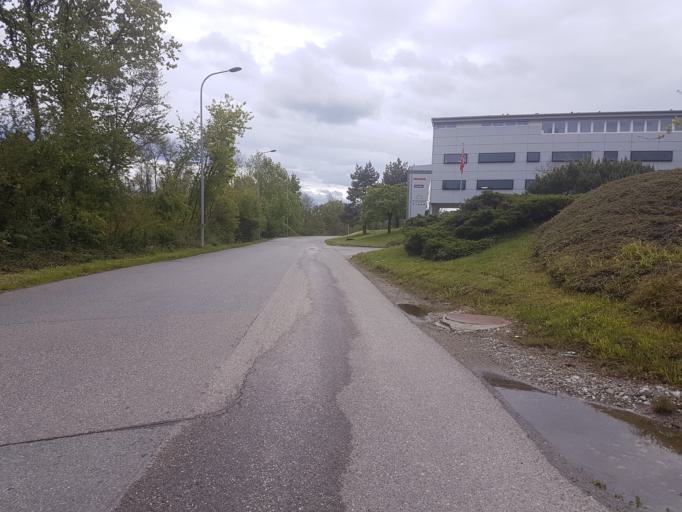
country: CH
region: Vaud
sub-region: Morges District
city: Preverenges
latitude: 46.5167
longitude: 6.5423
